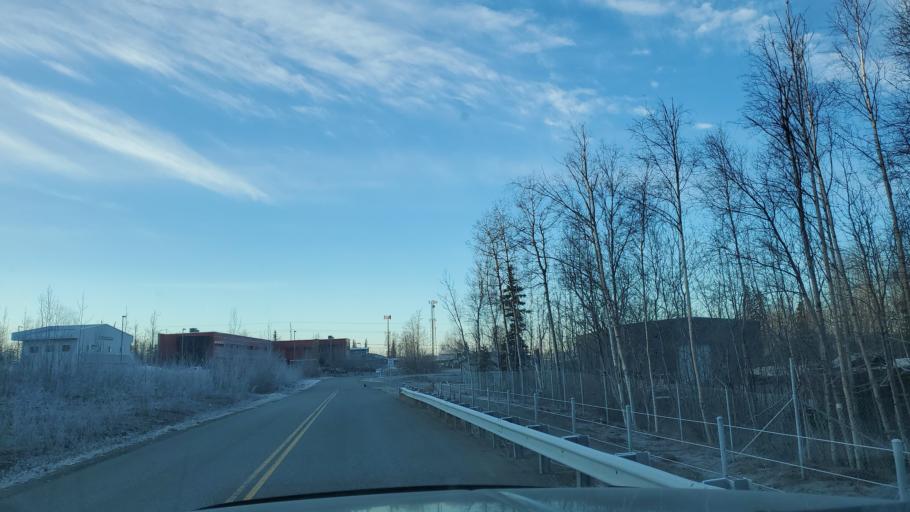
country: US
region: Alaska
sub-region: Matanuska-Susitna Borough
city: Wasilla
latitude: 61.5798
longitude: -149.4303
